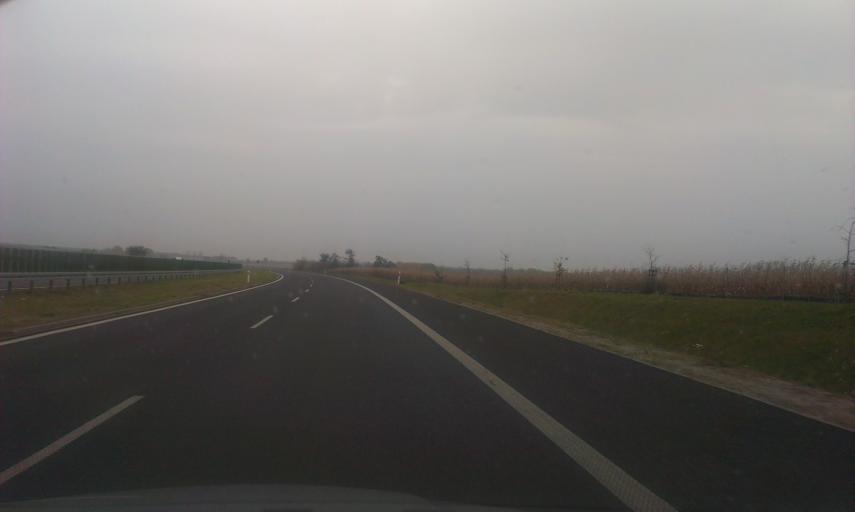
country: PL
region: Greater Poland Voivodeship
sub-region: Powiat poznanski
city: Zlotniki
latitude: 52.5139
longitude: 16.8100
